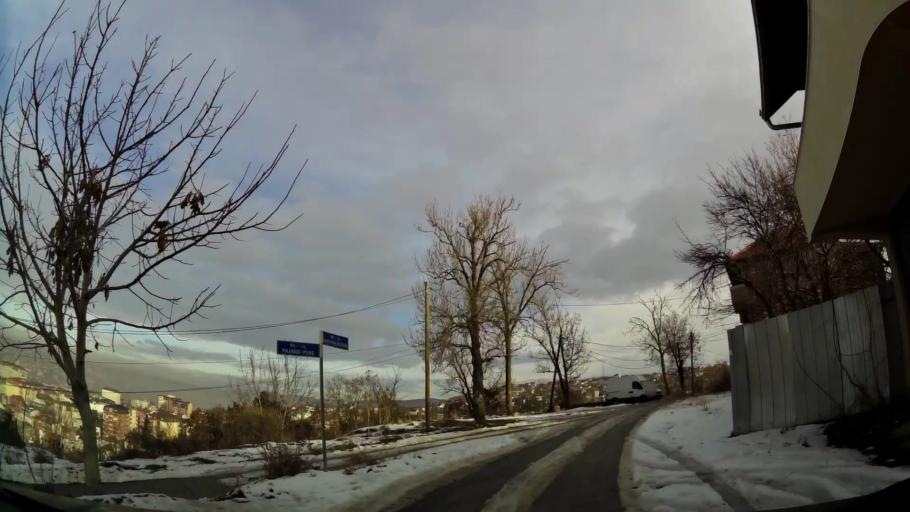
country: XK
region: Pristina
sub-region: Komuna e Prishtines
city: Pristina
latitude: 42.6637
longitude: 21.1735
